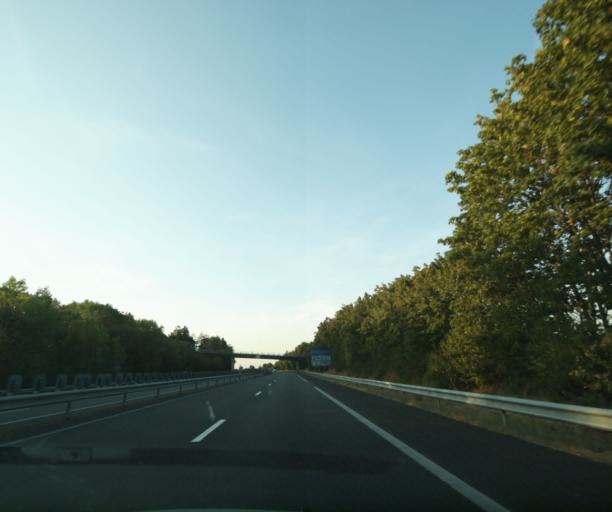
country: FR
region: Aquitaine
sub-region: Departement du Lot-et-Garonne
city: Boe
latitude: 44.1530
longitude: 0.6196
